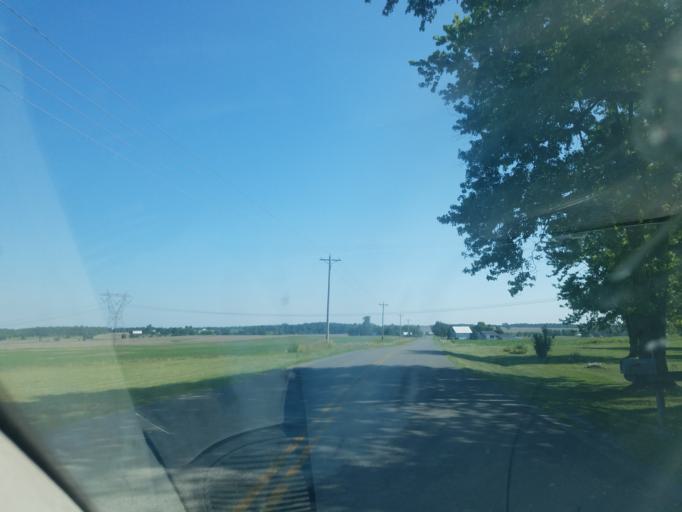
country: US
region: Ohio
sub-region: Logan County
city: Northwood
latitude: 40.4240
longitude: -83.6658
